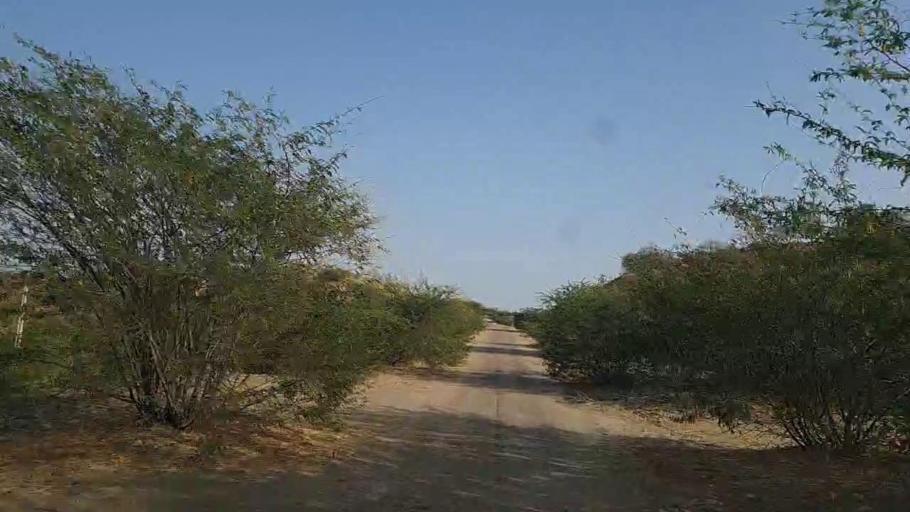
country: PK
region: Sindh
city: Diplo
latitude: 24.5977
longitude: 69.3856
